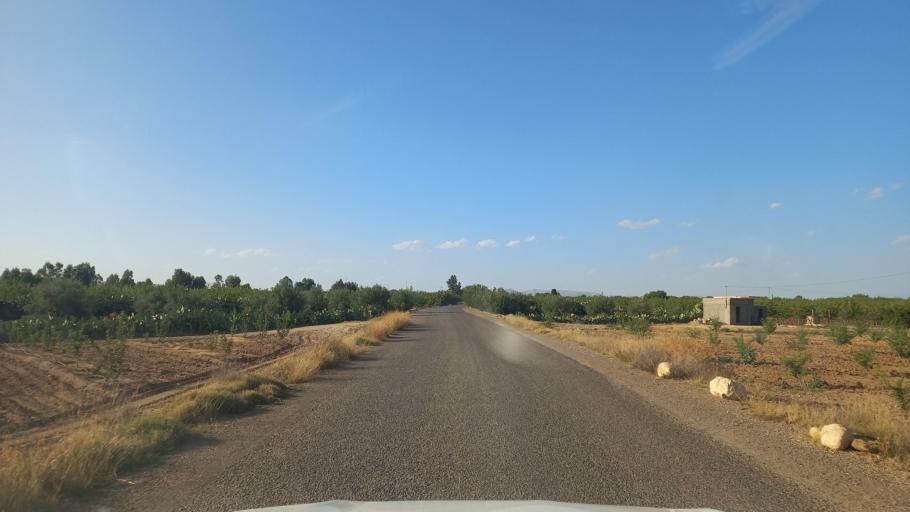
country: TN
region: Al Qasrayn
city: Kasserine
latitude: 35.2629
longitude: 9.0285
